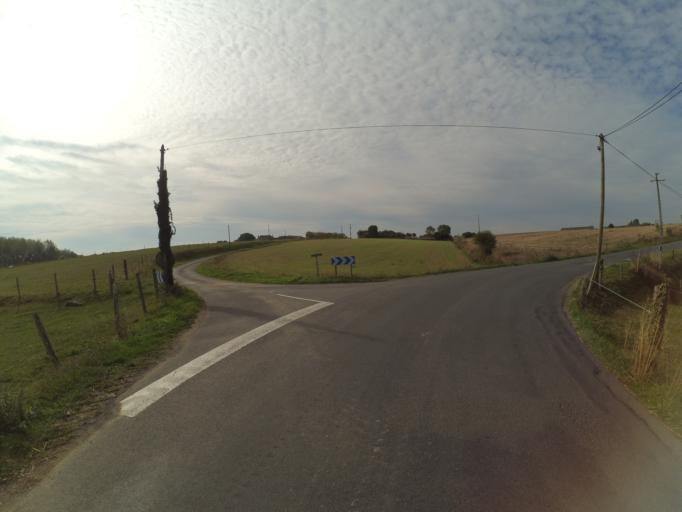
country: FR
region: Pays de la Loire
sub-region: Departement de Maine-et-Loire
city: La Jubaudiere
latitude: 47.1923
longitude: -0.8909
